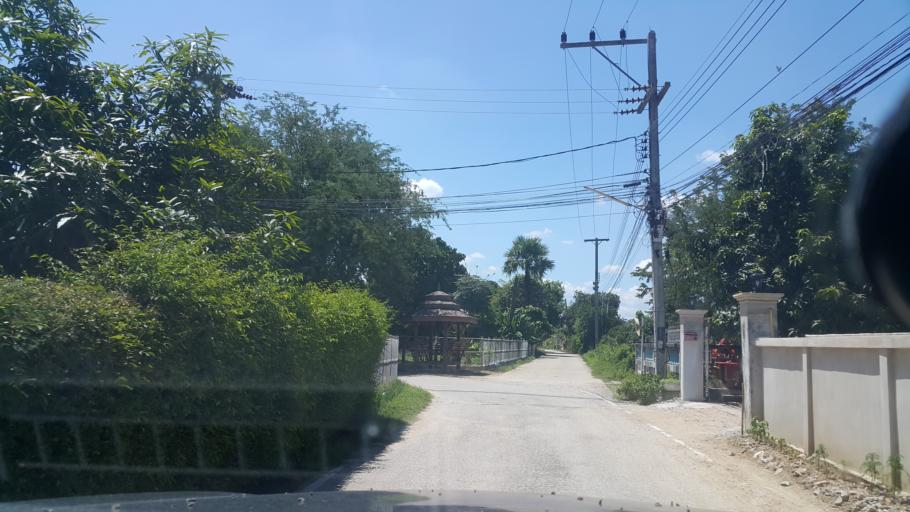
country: TH
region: Chiang Mai
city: San Kamphaeng
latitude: 18.7039
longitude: 99.1579
